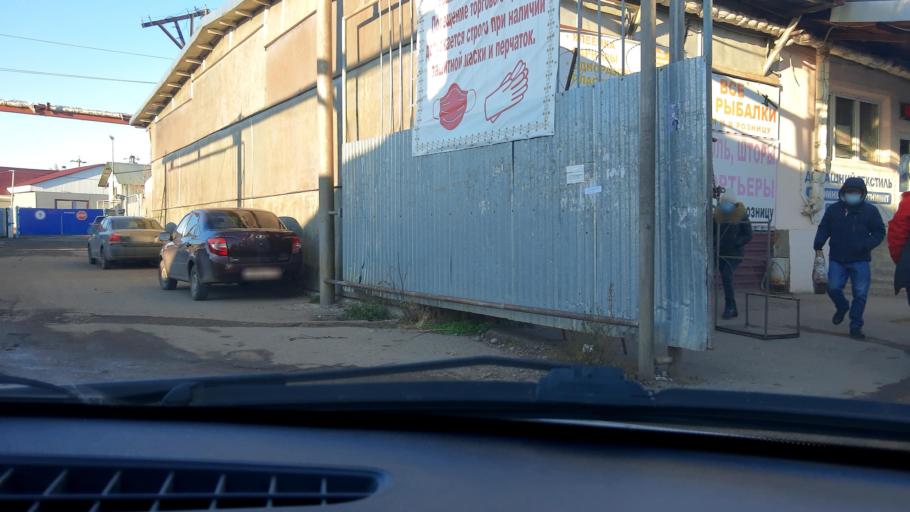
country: RU
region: Bashkortostan
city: Mikhaylovka
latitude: 54.6940
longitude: 55.8432
